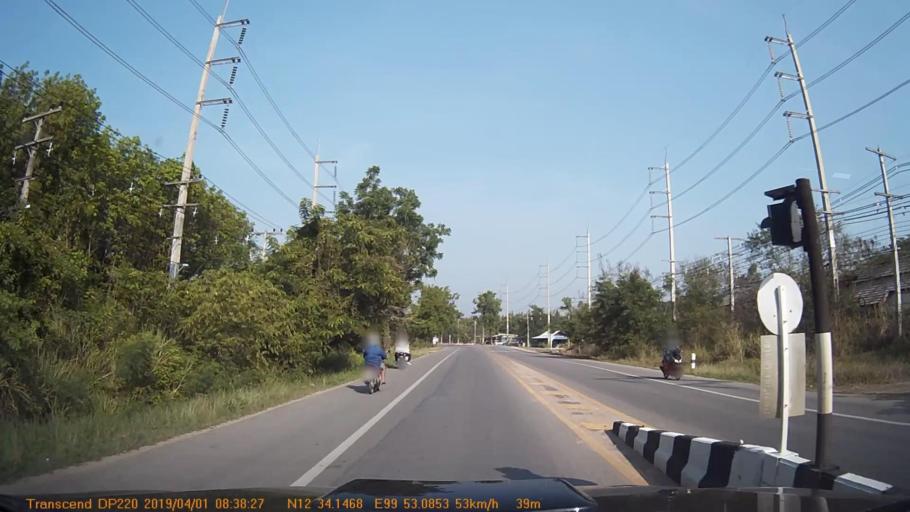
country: TH
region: Prachuap Khiri Khan
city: Hua Hin
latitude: 12.5692
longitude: 99.8846
